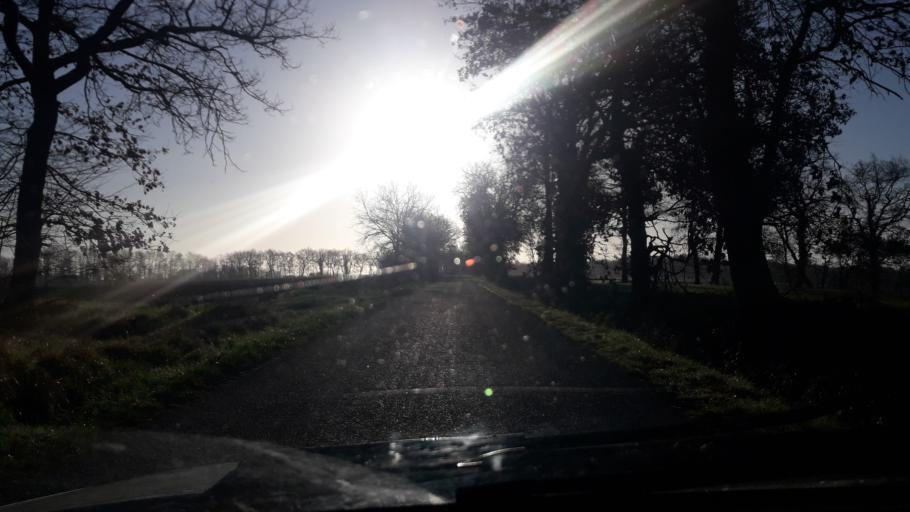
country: FR
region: Midi-Pyrenees
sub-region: Departement du Gers
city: Gimont
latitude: 43.6492
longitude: 0.9911
